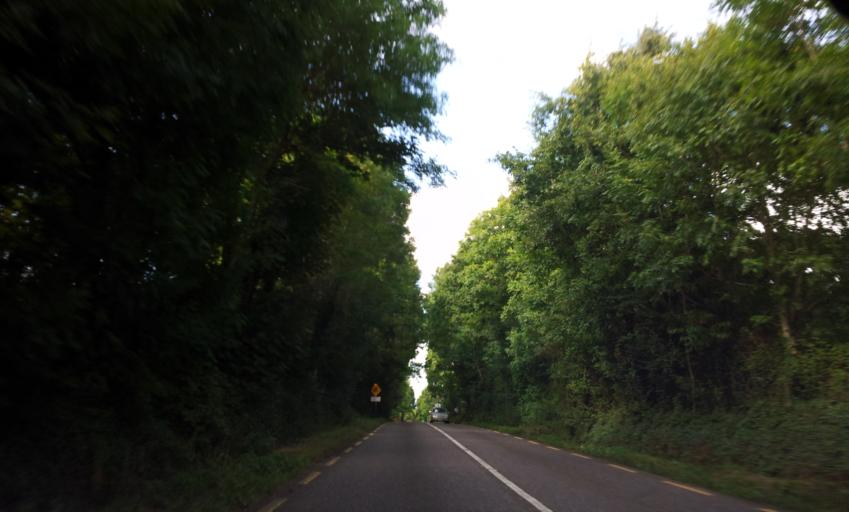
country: IE
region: Munster
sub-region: County Cork
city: Macroom
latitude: 51.8789
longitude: -8.9323
